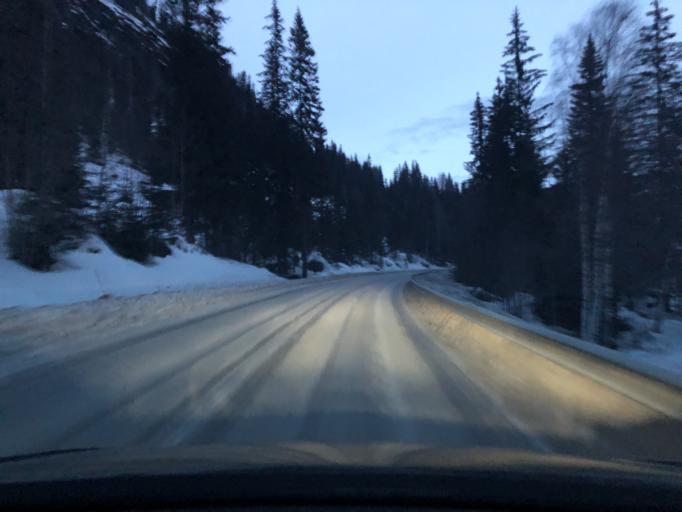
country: NO
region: Oppland
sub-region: Nord-Aurdal
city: Fagernes
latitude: 61.0014
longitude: 9.2092
